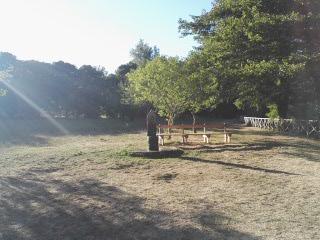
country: IT
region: Calabria
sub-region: Provincia di Vibo-Valentia
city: Mongiana
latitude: 38.5209
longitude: 16.3046
